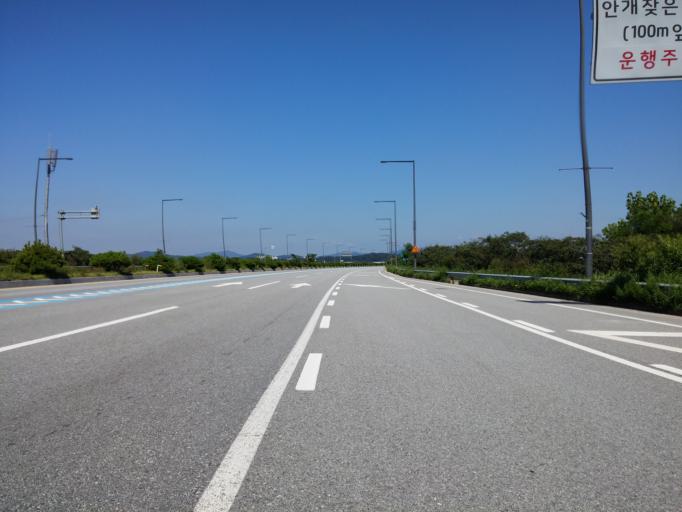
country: KR
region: Daejeon
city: Songgang-dong
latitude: 36.5476
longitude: 127.3015
